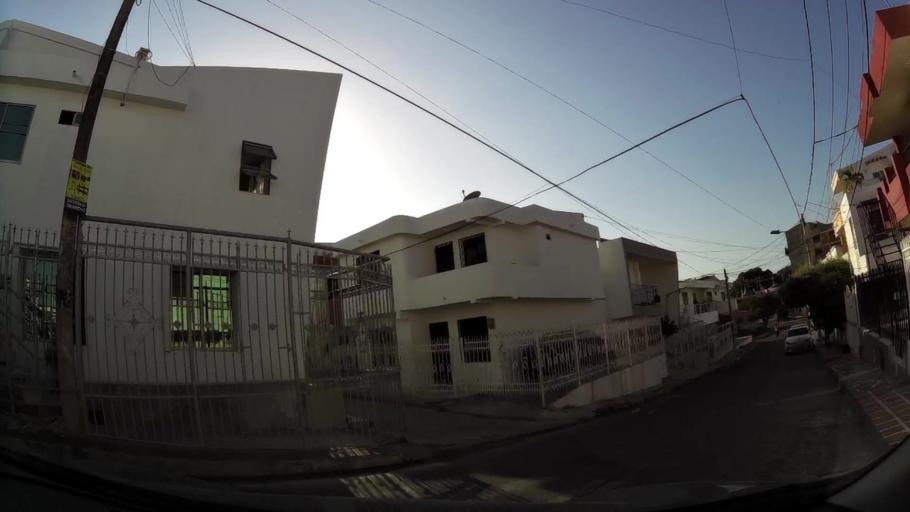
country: CO
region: Bolivar
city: Cartagena
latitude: 10.3980
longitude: -75.4820
